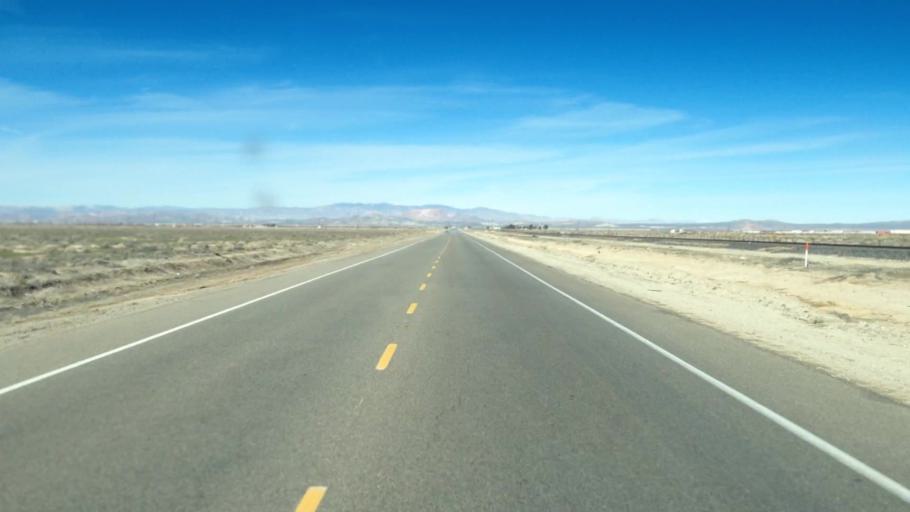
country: US
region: California
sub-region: Los Angeles County
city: Lancaster
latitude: 34.7412
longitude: -118.1422
